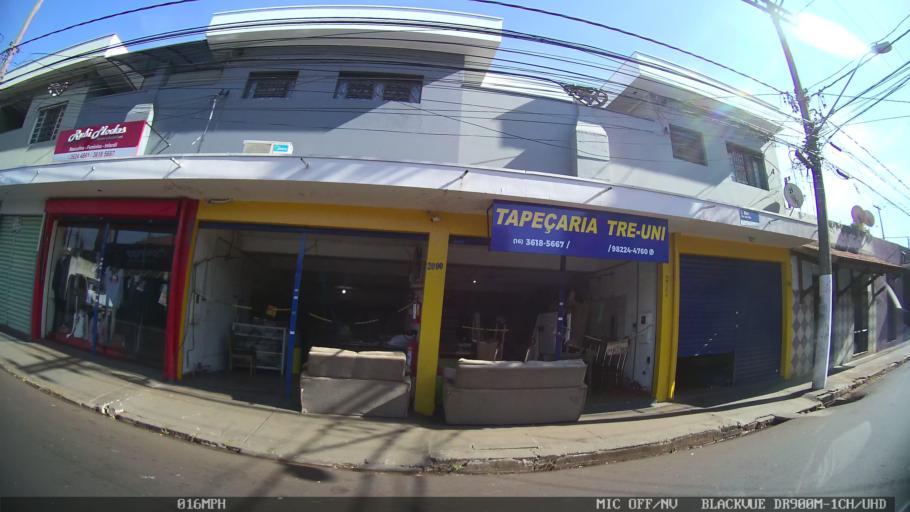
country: BR
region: Sao Paulo
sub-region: Ribeirao Preto
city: Ribeirao Preto
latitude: -21.1751
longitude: -47.7835
